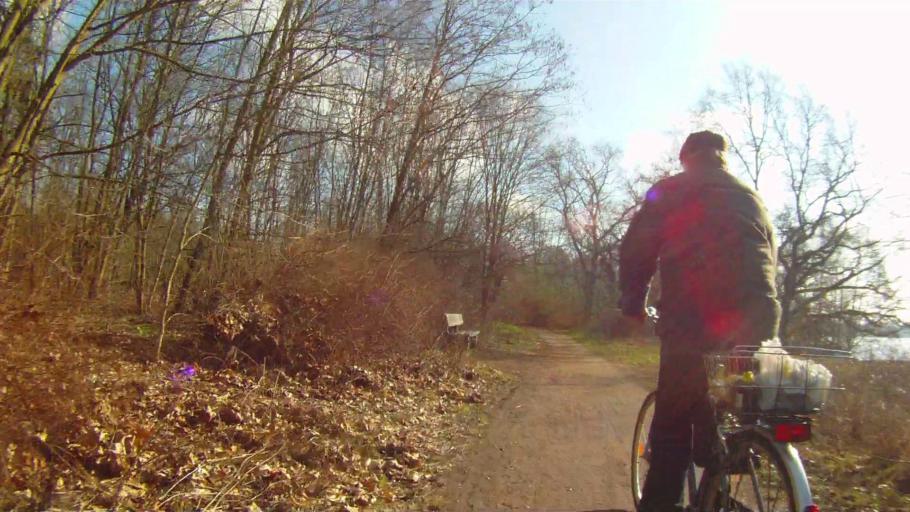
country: DE
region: Brandenburg
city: Erkner
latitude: 52.4274
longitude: 13.7343
